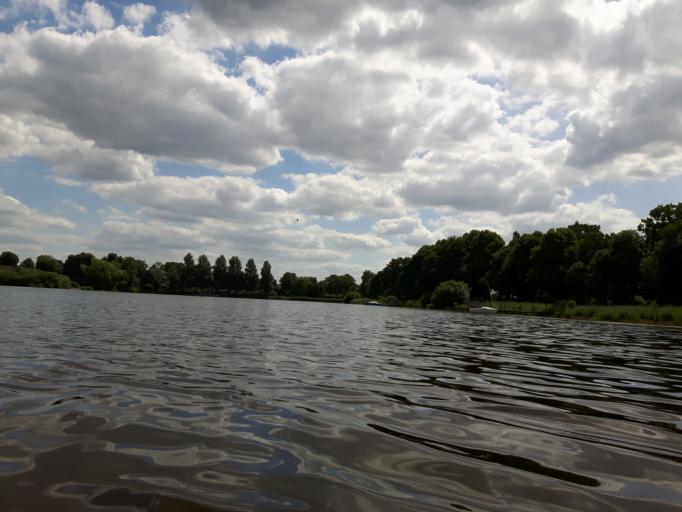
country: DE
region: Schleswig-Holstein
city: Muhbrook
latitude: 54.1345
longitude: 9.9880
